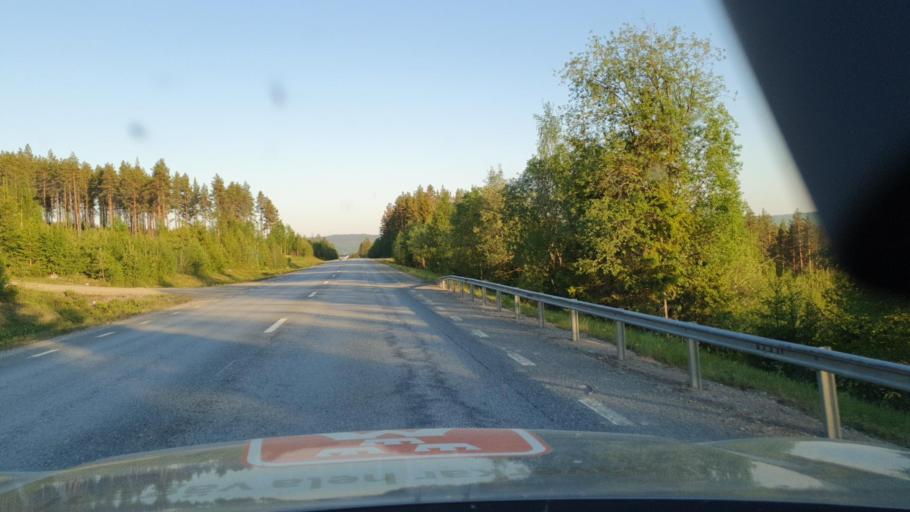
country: SE
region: Vaesternorrland
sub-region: Solleftea Kommun
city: Solleftea
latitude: 63.3753
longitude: 16.9995
